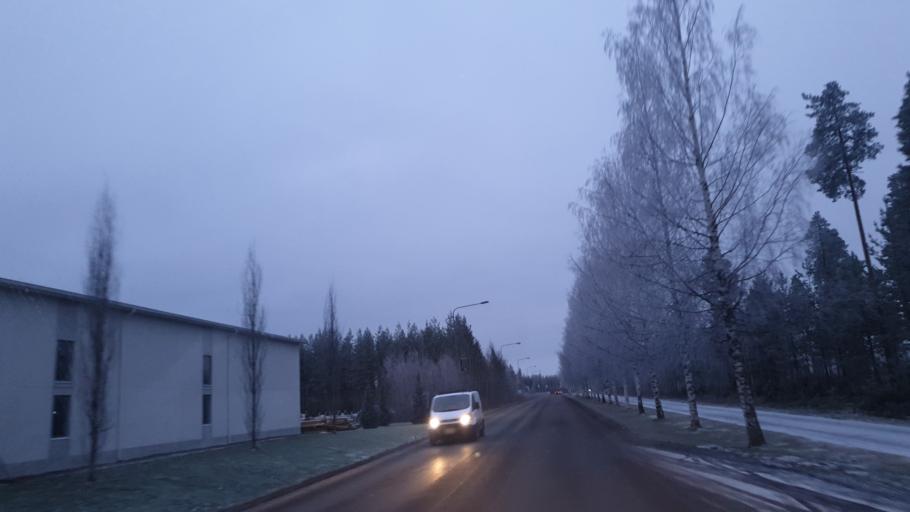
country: FI
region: Southern Ostrobothnia
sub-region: Seinaejoki
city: Nurmo
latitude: 62.7822
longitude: 22.8990
